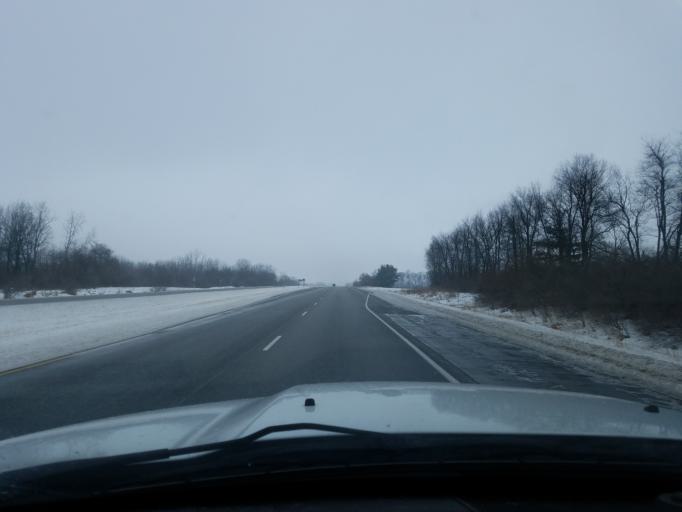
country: US
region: Indiana
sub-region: Fulton County
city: Rochester
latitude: 40.9368
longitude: -86.1683
